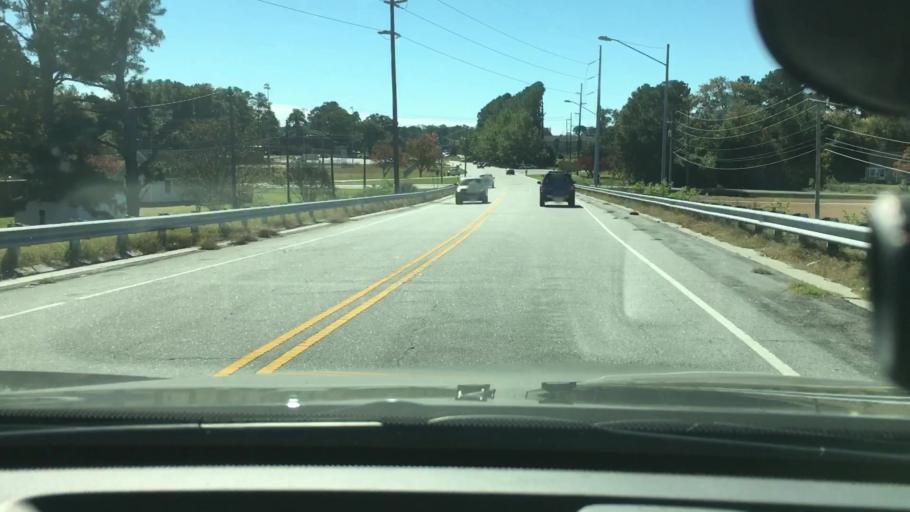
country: US
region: North Carolina
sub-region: Edgecombe County
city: Tarboro
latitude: 35.9083
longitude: -77.5628
